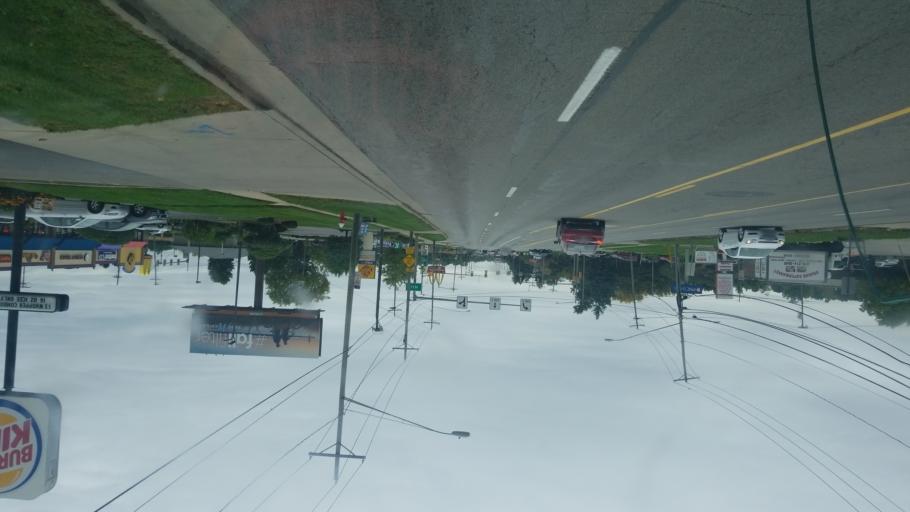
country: US
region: Ohio
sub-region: Lucas County
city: Ottawa Hills
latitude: 41.6373
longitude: -83.6644
